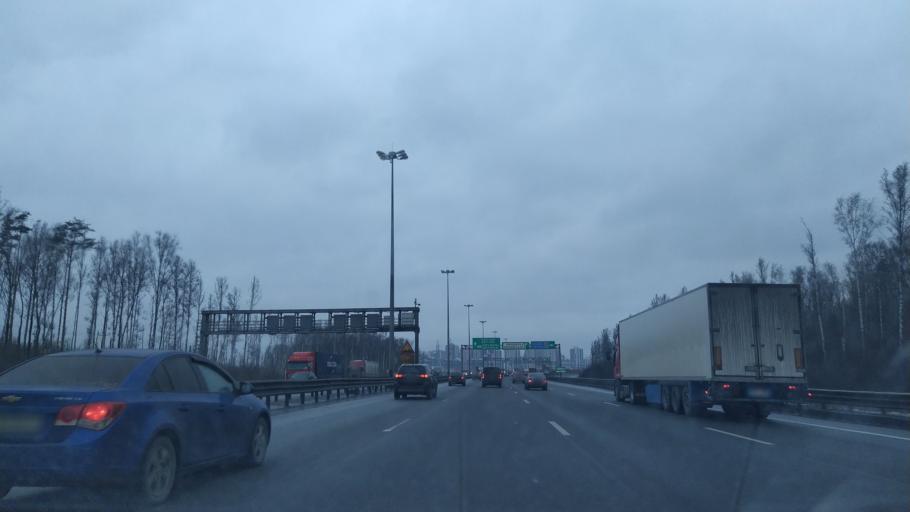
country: RU
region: Leningrad
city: Rybatskoye
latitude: 59.8842
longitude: 30.5263
